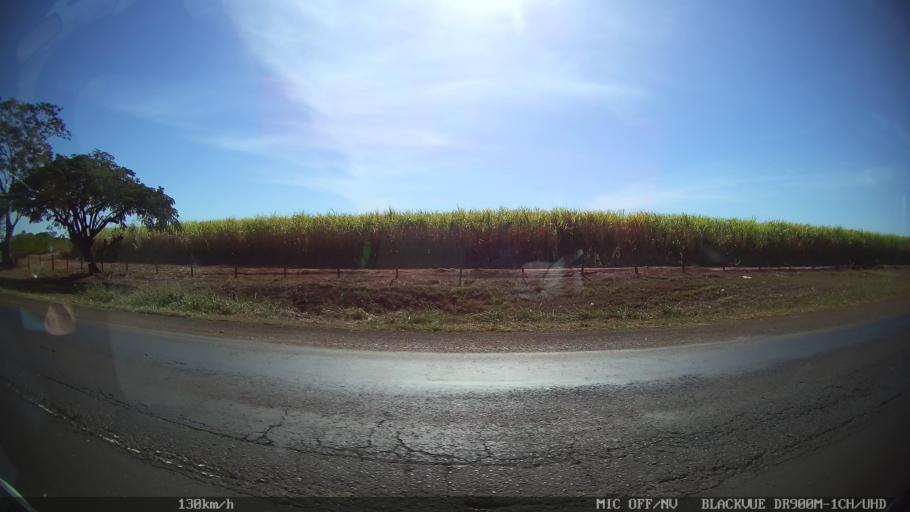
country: BR
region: Sao Paulo
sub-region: Barretos
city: Barretos
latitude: -20.5657
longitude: -48.6617
